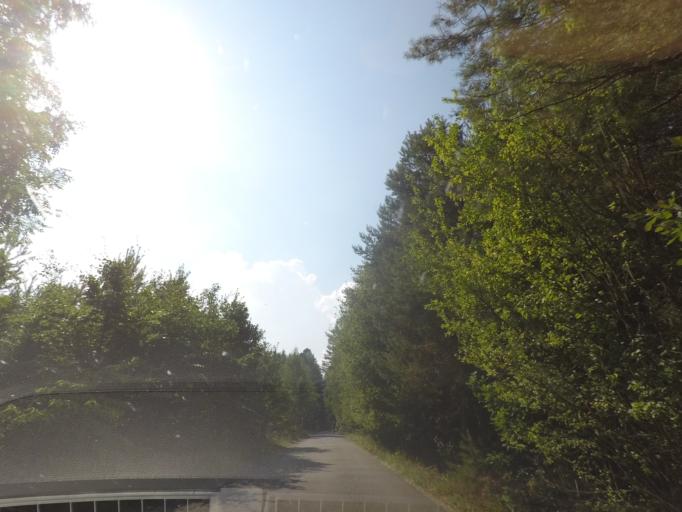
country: CZ
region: Pardubicky
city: Horni Jeleni
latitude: 50.0642
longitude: 16.0772
